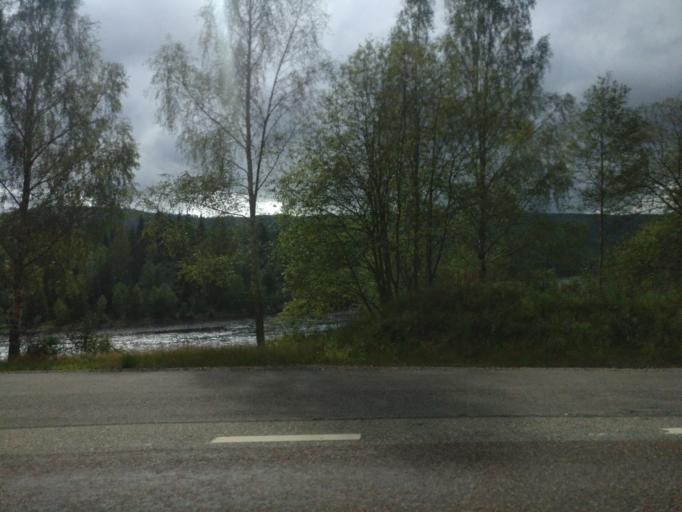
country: SE
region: Vaermland
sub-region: Torsby Kommun
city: Torsby
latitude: 60.7506
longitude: 12.8072
